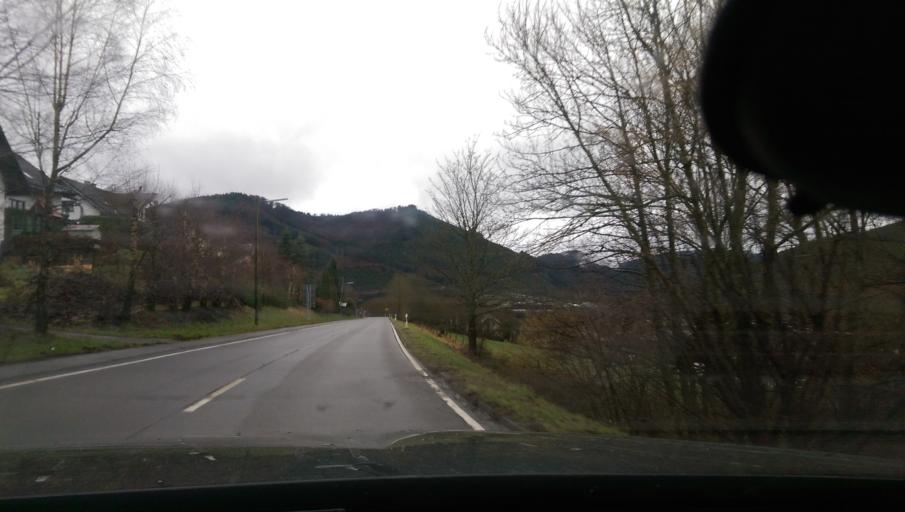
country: DE
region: North Rhine-Westphalia
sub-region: Regierungsbezirk Arnsberg
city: Finnentrop
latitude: 51.2244
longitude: 7.9583
